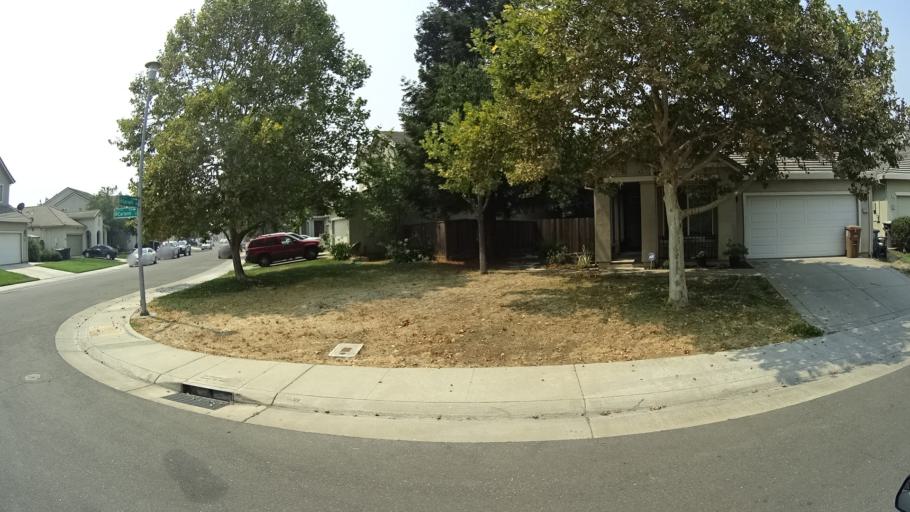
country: US
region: California
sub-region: Sacramento County
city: Laguna
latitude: 38.4040
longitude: -121.4348
